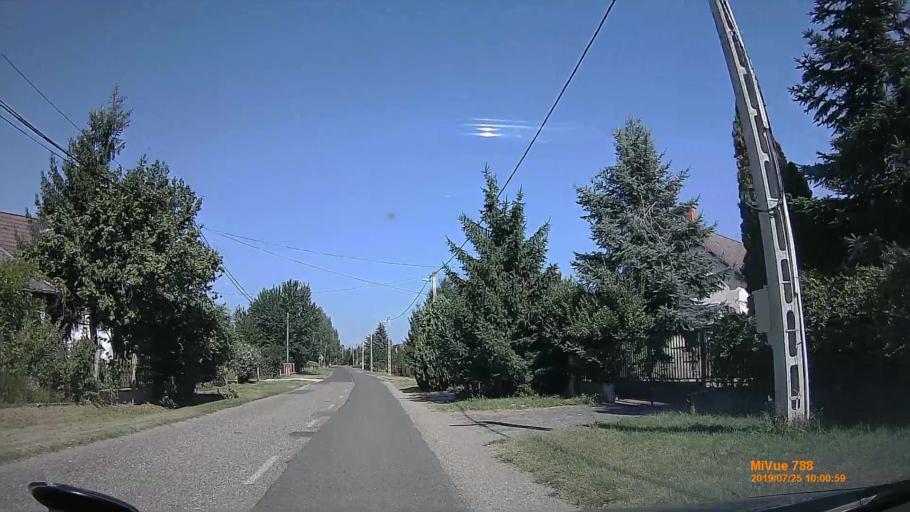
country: HU
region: Szabolcs-Szatmar-Bereg
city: Kotaj
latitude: 48.0320
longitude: 21.7535
